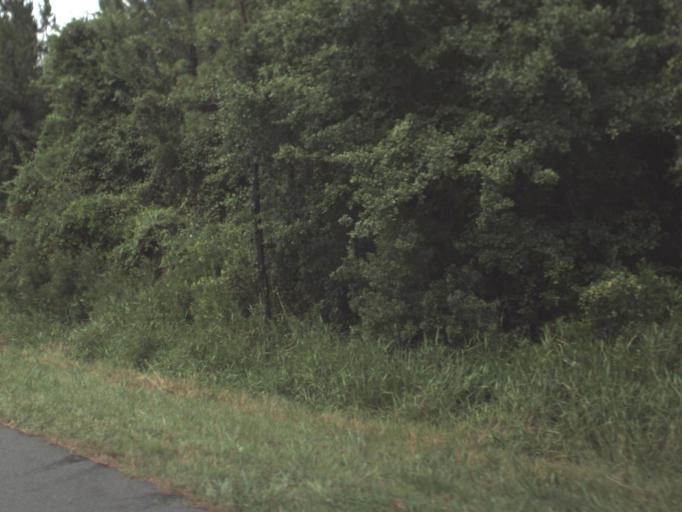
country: US
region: Florida
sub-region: Hamilton County
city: Jasper
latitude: 30.5857
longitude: -82.6789
